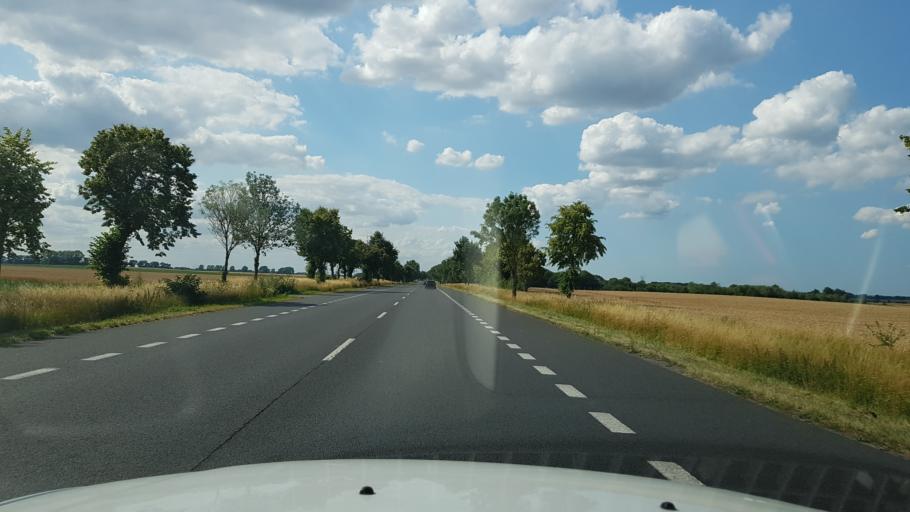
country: PL
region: West Pomeranian Voivodeship
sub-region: Powiat pyrzycki
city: Pyrzyce
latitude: 53.1619
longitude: 14.8684
